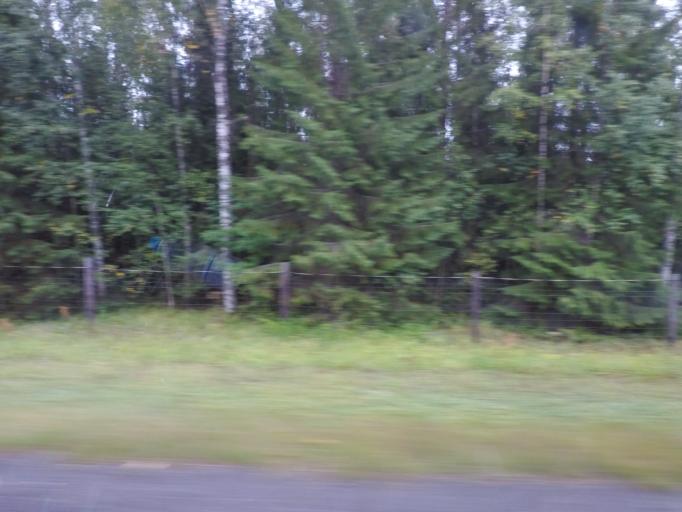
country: FI
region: Southern Savonia
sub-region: Pieksaemaeki
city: Juva
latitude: 62.0002
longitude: 27.8025
